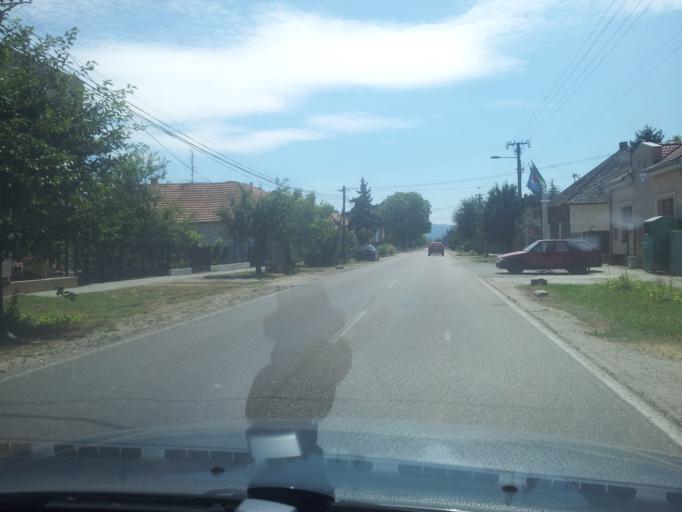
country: SK
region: Nitriansky
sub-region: Okres Nove Zamky
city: Sturovo
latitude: 47.8144
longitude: 18.6982
